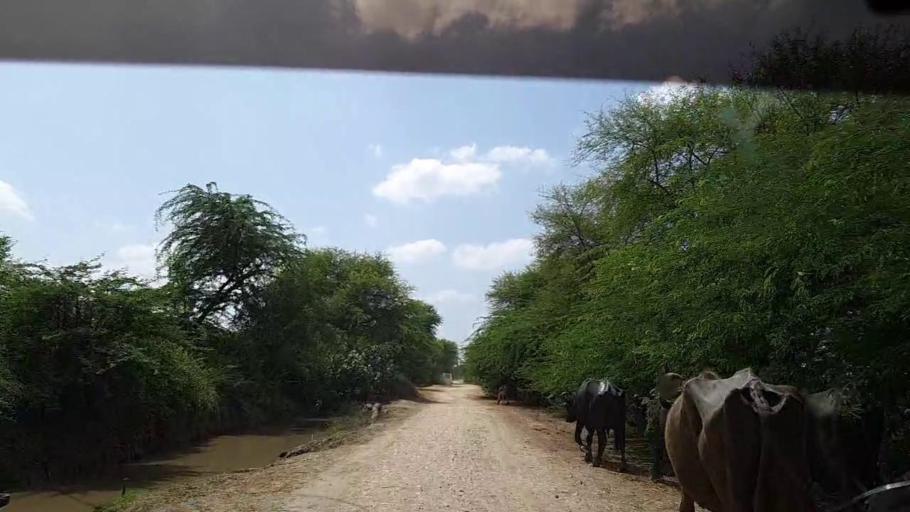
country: PK
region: Sindh
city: Badin
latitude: 24.5681
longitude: 68.7601
